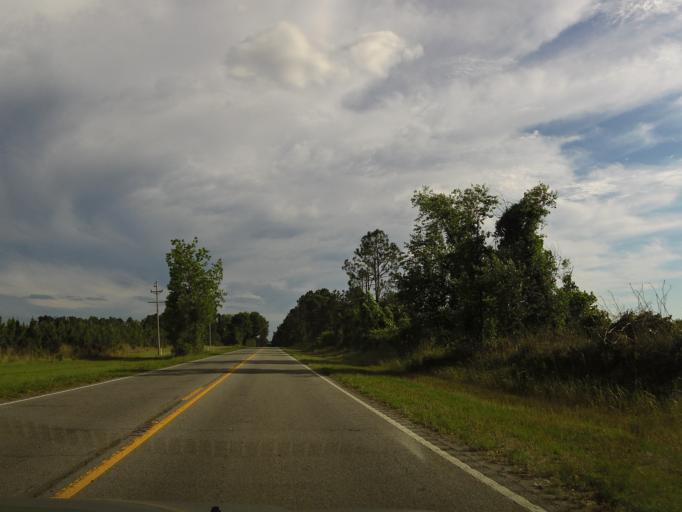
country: US
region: South Carolina
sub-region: Hampton County
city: Estill
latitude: 32.7780
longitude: -81.2409
